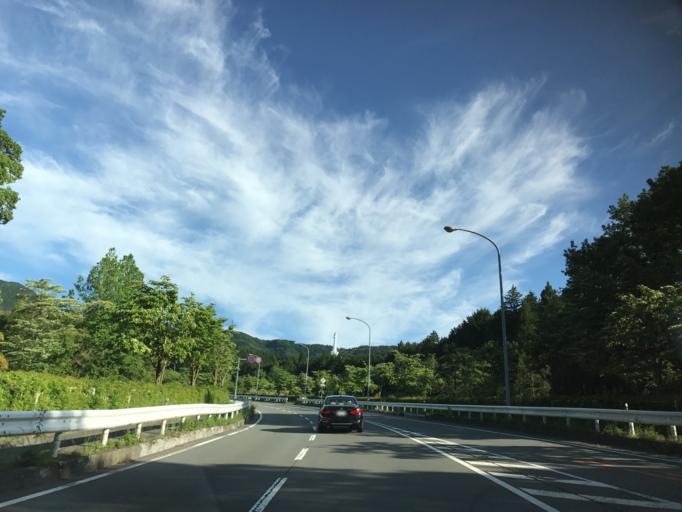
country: JP
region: Shizuoka
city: Gotemba
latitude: 35.2883
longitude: 138.9556
